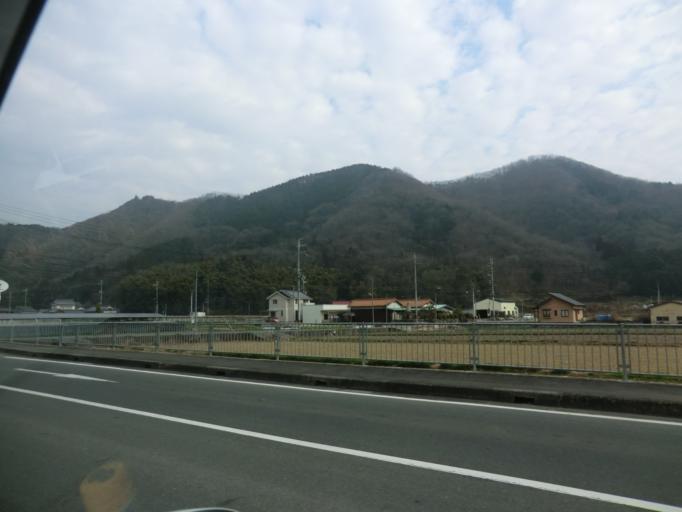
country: JP
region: Hyogo
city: Yamazakicho-nakabirose
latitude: 34.9408
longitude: 134.4732
